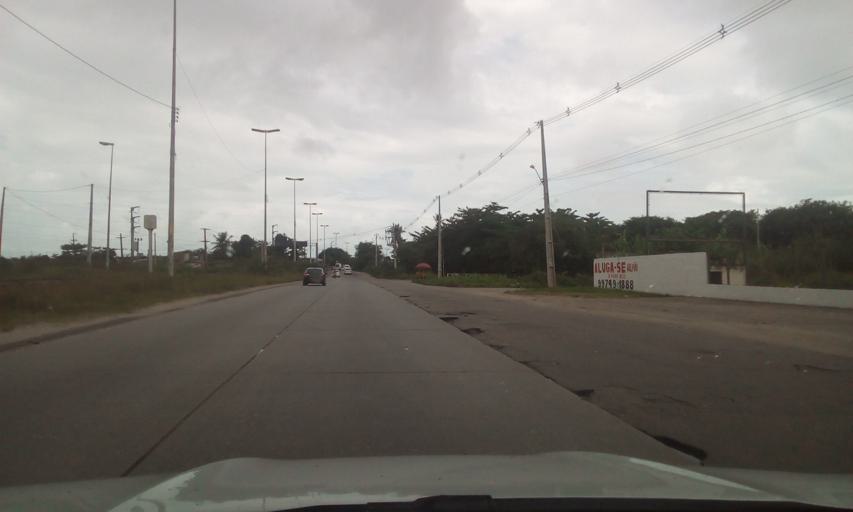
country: BR
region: Pernambuco
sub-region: Recife
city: Recife
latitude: -8.0759
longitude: -34.9361
